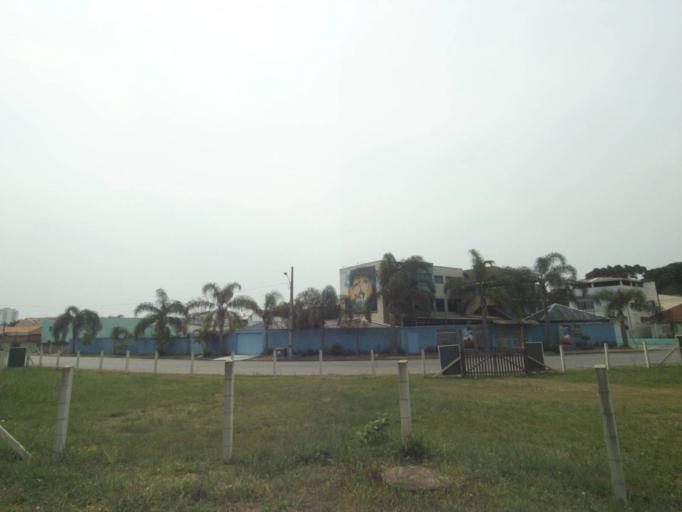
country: BR
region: Parana
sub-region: Sao Jose Dos Pinhais
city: Sao Jose dos Pinhais
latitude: -25.5258
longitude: -49.2807
